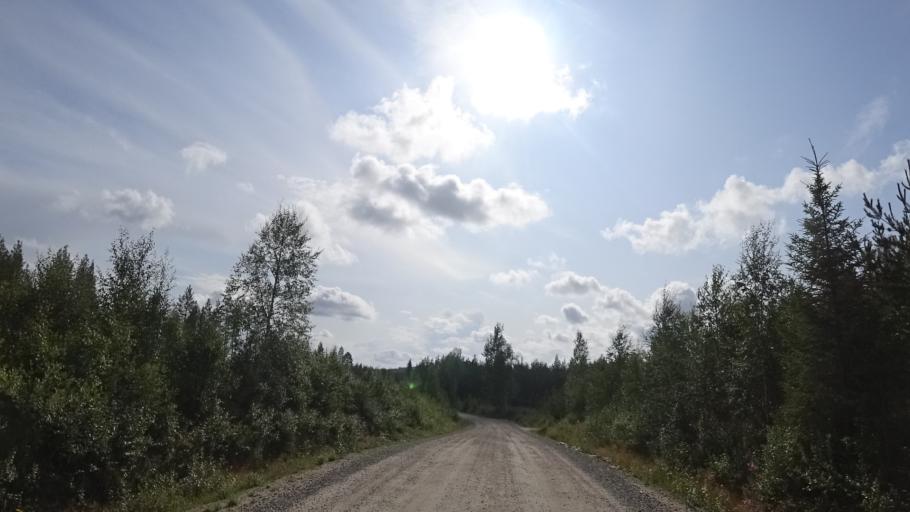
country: FI
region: North Karelia
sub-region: Pielisen Karjala
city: Lieksa
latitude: 63.5805
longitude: 30.1293
